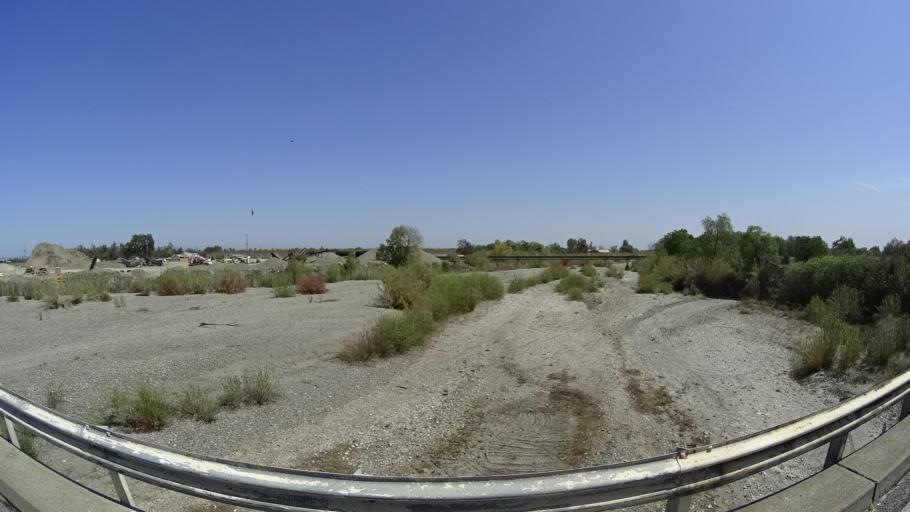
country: US
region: California
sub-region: Glenn County
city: Orland
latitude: 39.7661
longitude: -122.1969
